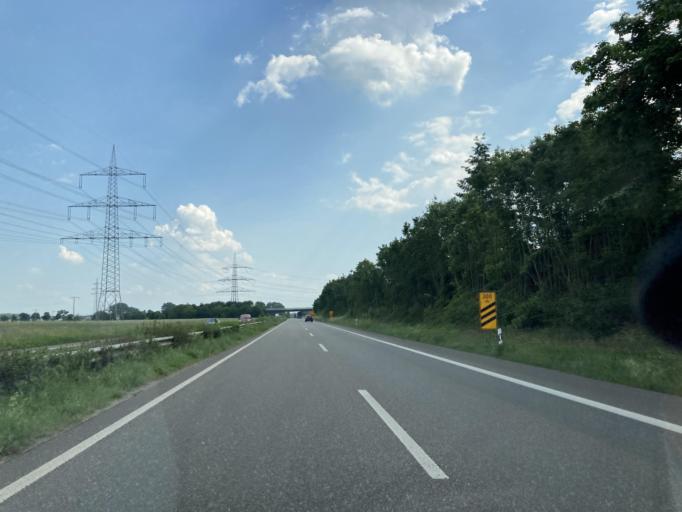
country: DE
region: Rheinland-Pfalz
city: Kuhardt
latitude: 49.1544
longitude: 8.3030
